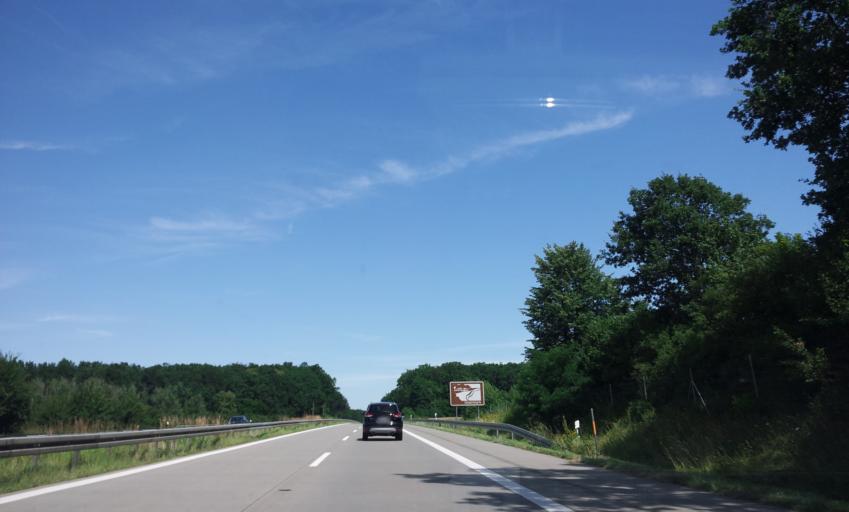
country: DE
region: Brandenburg
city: Althuttendorf
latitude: 52.9839
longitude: 13.8199
